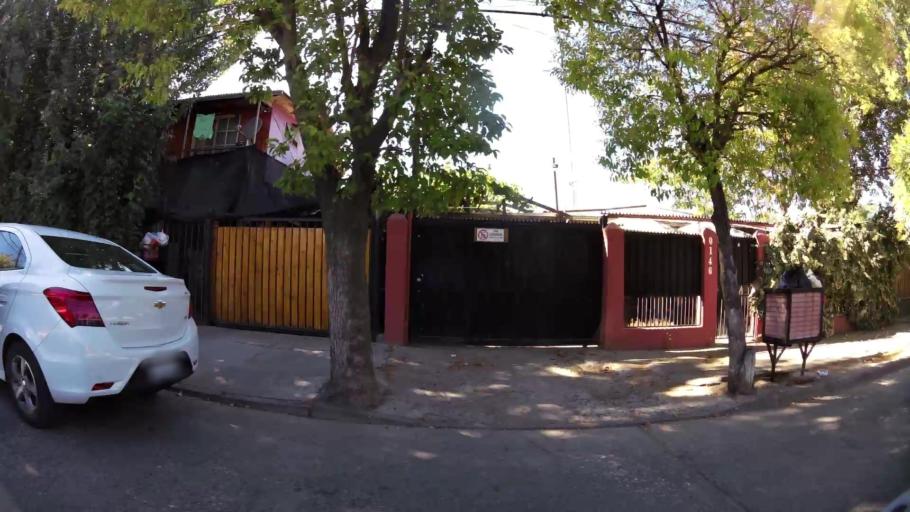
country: CL
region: O'Higgins
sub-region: Provincia de Cachapoal
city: Rancagua
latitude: -34.1715
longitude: -70.7023
